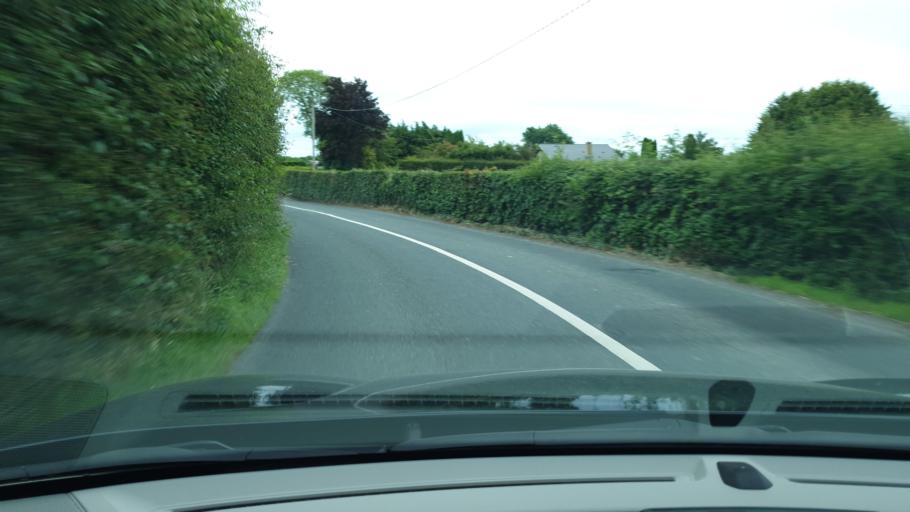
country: IE
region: Leinster
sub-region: An Mhi
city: Dunboyne
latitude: 53.4341
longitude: -6.4837
